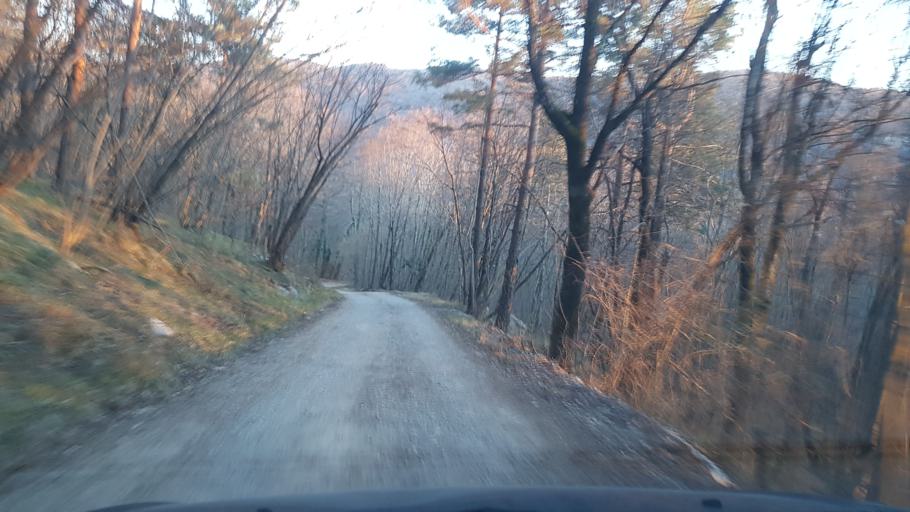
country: SI
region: Nova Gorica
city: Kromberk
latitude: 46.0097
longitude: 13.7011
